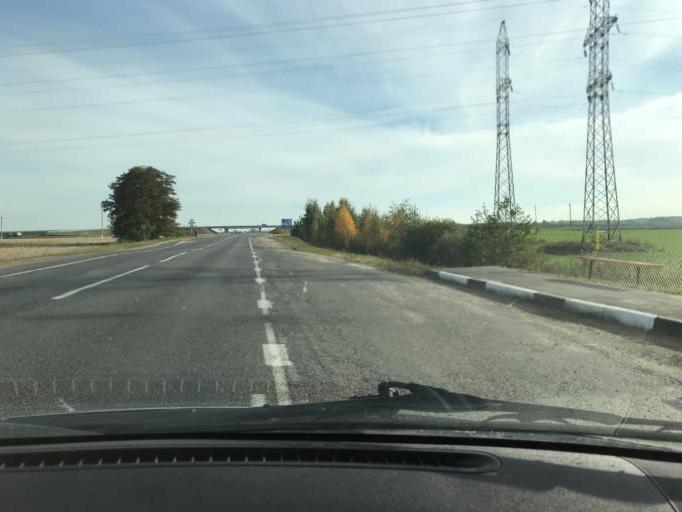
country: BY
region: Brest
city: Asnyezhytsy
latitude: 52.1891
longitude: 26.0756
